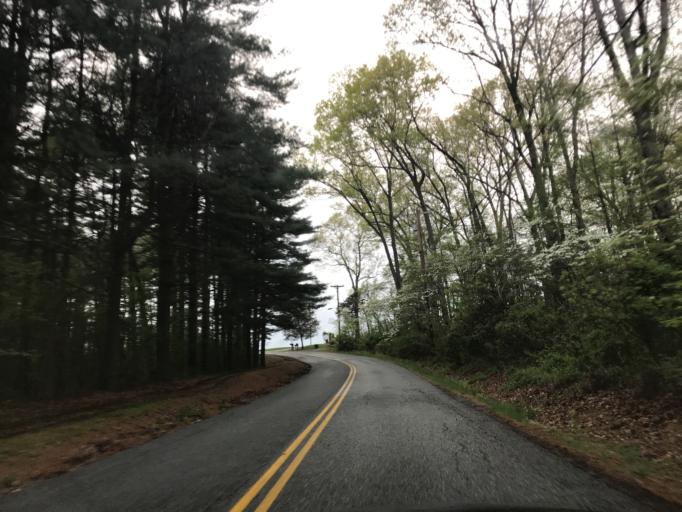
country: US
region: Maryland
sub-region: Harford County
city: Jarrettsville
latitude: 39.6689
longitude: -76.4723
